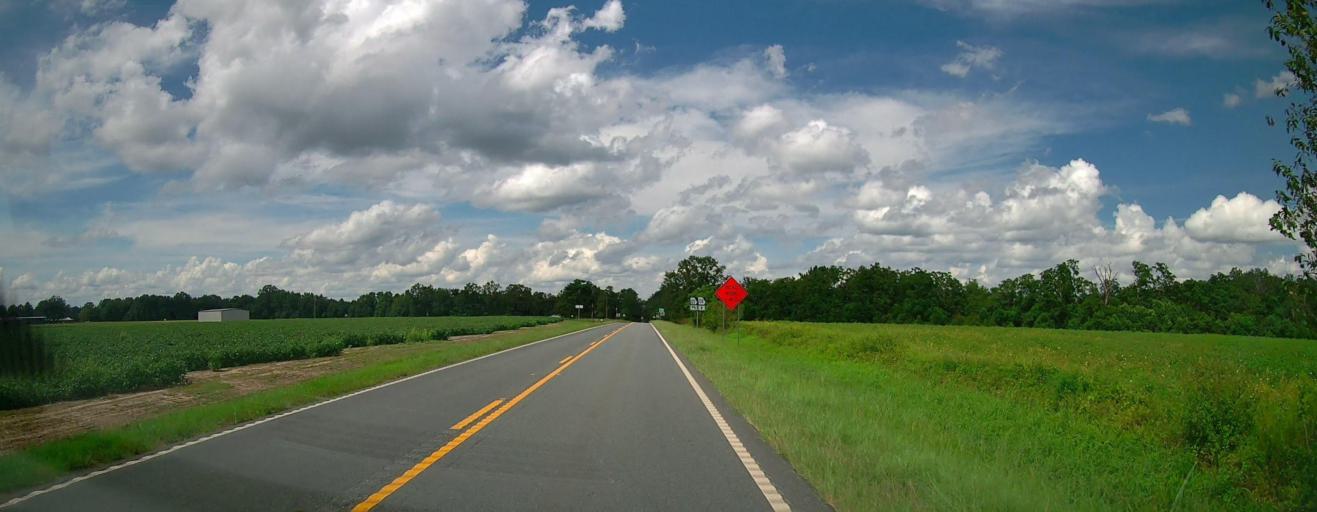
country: US
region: Georgia
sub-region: Taylor County
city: Reynolds
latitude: 32.4379
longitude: -84.0762
